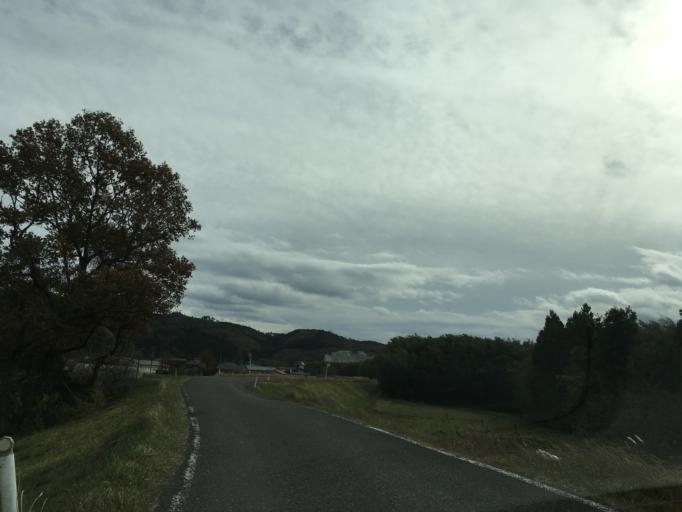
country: JP
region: Iwate
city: Ichinoseki
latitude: 38.7587
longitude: 141.2774
